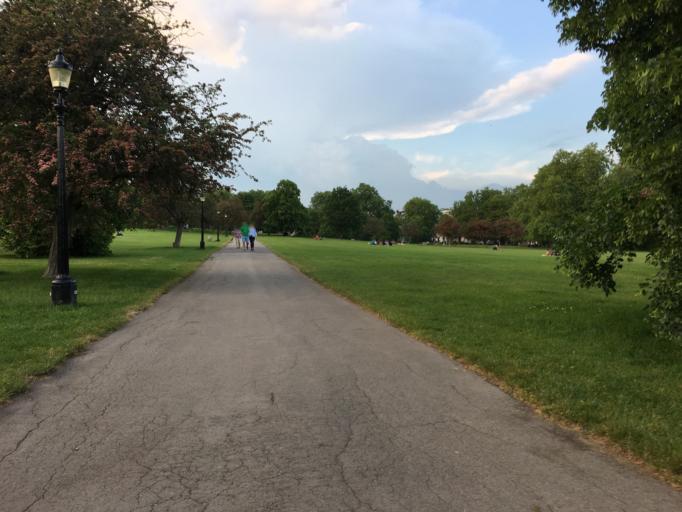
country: GB
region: England
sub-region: Greater London
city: Camden Town
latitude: 51.5378
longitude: -0.1588
